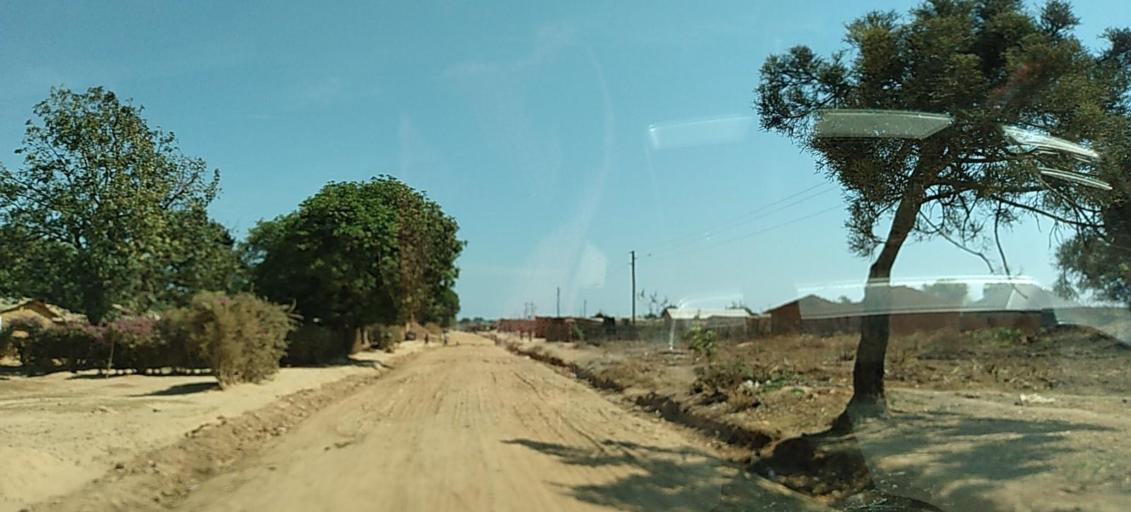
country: ZM
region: Copperbelt
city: Chililabombwe
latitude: -12.3302
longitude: 27.8602
